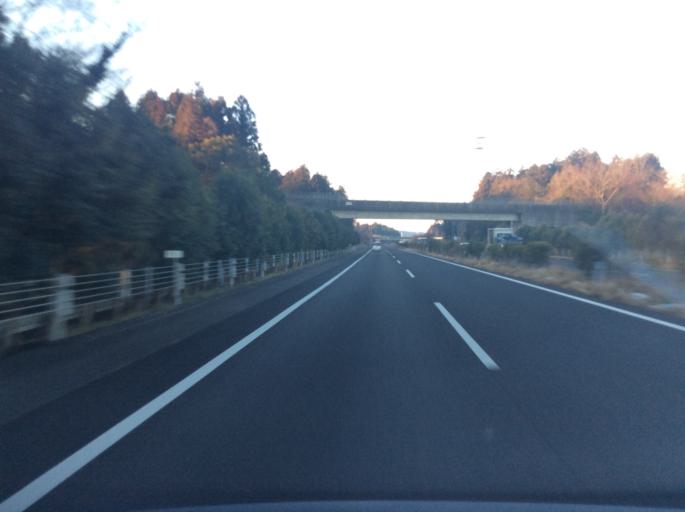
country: JP
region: Ibaraki
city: Hitachi-Naka
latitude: 36.4396
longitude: 140.4541
